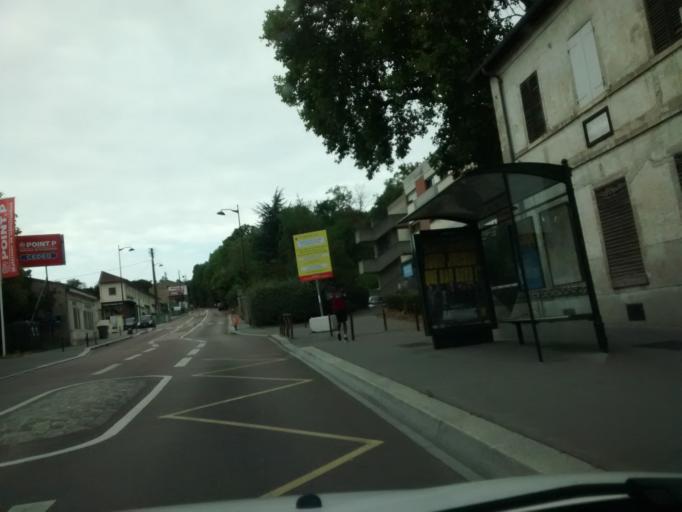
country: FR
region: Ile-de-France
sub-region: Departement des Yvelines
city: Versailles
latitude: 48.7943
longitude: 2.1377
